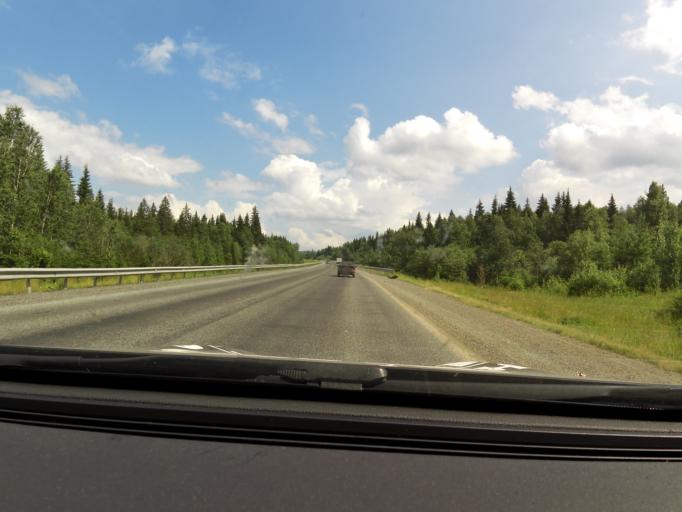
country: RU
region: Sverdlovsk
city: Arti
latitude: 56.7886
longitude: 58.5064
